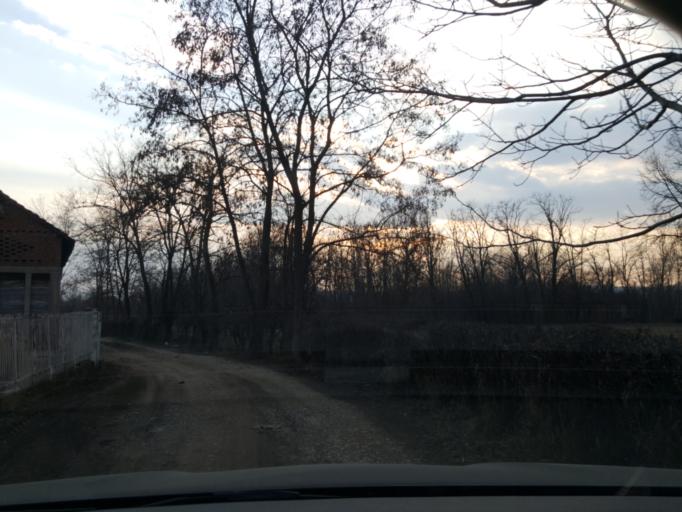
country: RS
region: Central Serbia
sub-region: Nisavski Okrug
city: Razanj
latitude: 43.5921
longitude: 21.6159
